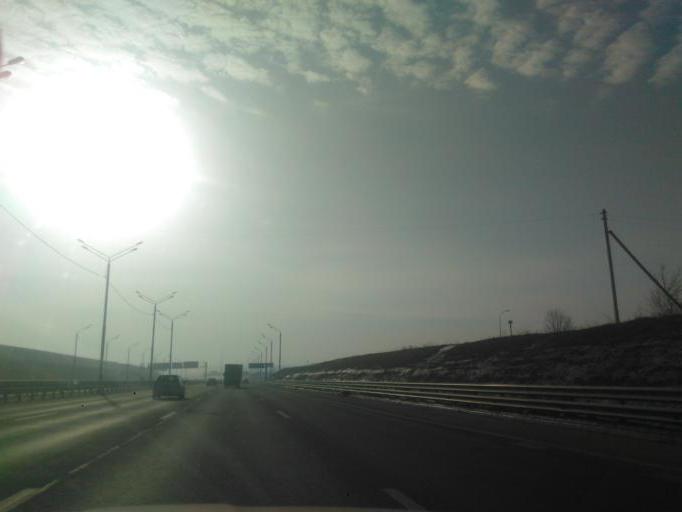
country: RU
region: Moskovskaya
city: Pavlovskaya Sloboda
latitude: 55.8060
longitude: 37.0355
